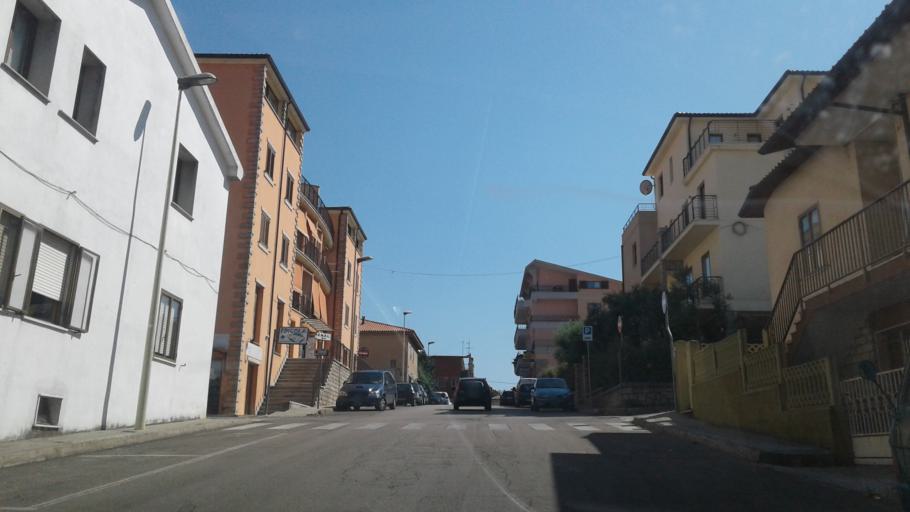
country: IT
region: Sardinia
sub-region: Provincia di Olbia-Tempio
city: Tempio Pausania
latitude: 40.8979
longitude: 9.1080
